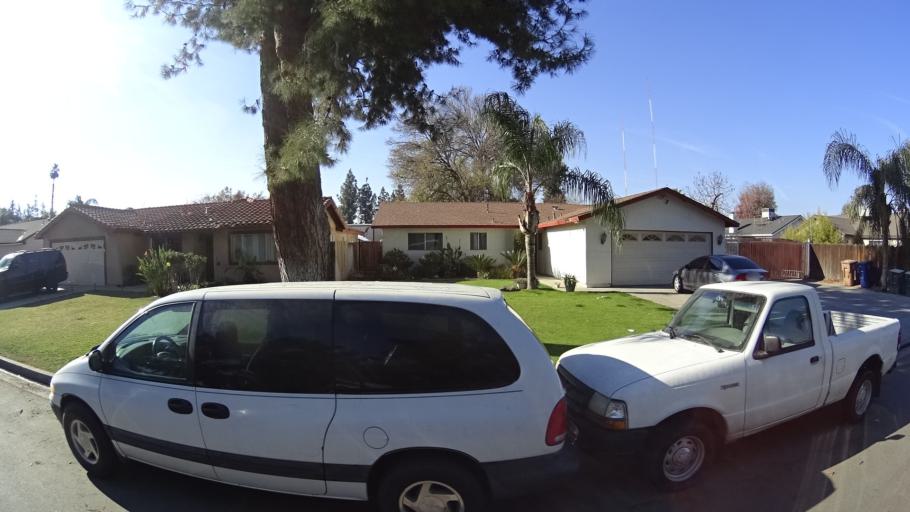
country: US
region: California
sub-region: Kern County
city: Greenfield
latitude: 35.3067
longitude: -119.0413
